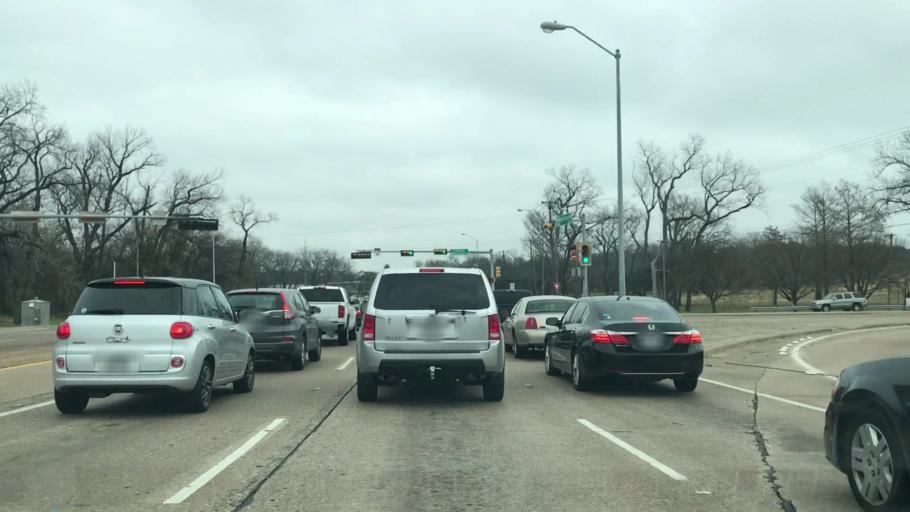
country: US
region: Texas
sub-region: Dallas County
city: Highland Park
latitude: 32.8606
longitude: -96.7202
